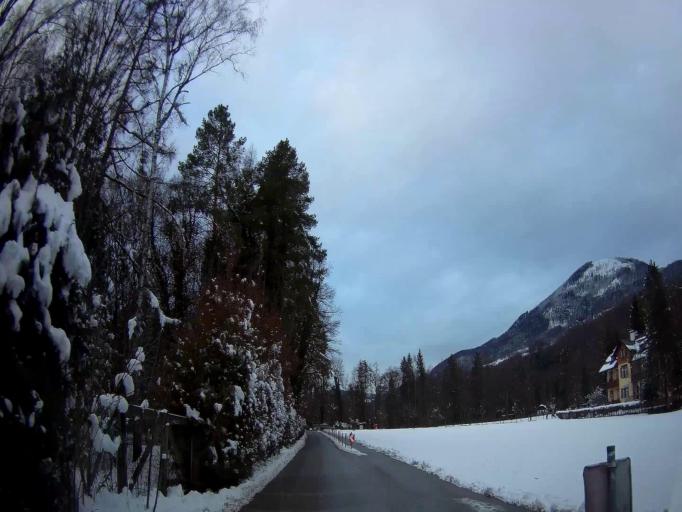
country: AT
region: Salzburg
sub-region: Politischer Bezirk Salzburg-Umgebung
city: Elsbethen
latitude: 47.7837
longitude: 13.0900
